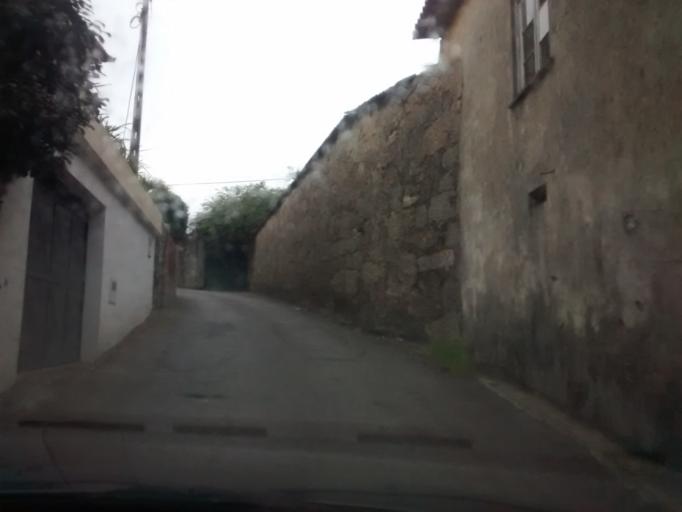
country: PT
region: Braga
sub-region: Vila Nova de Famalicao
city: Vila Nova de Famalicao
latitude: 41.4530
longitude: -8.5318
